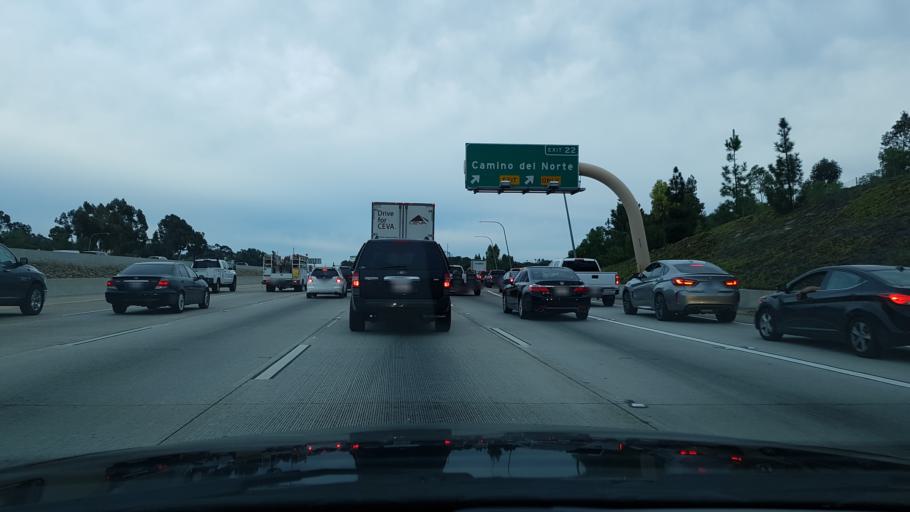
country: US
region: California
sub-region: San Diego County
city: Poway
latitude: 33.0024
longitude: -117.0821
